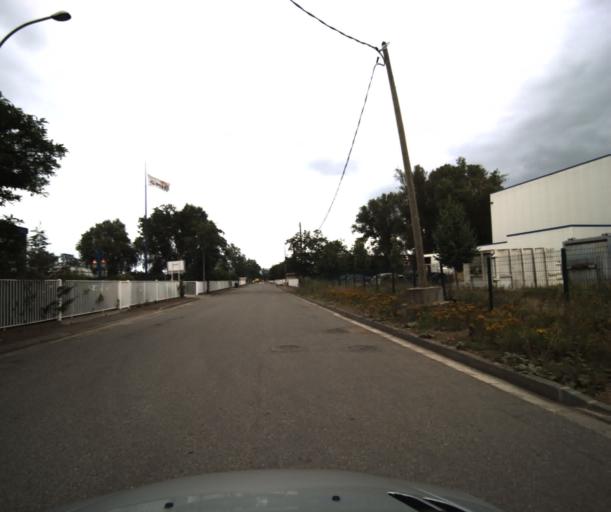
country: FR
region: Midi-Pyrenees
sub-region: Departement de la Haute-Garonne
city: Pinsaguel
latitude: 43.5311
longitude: 1.3763
